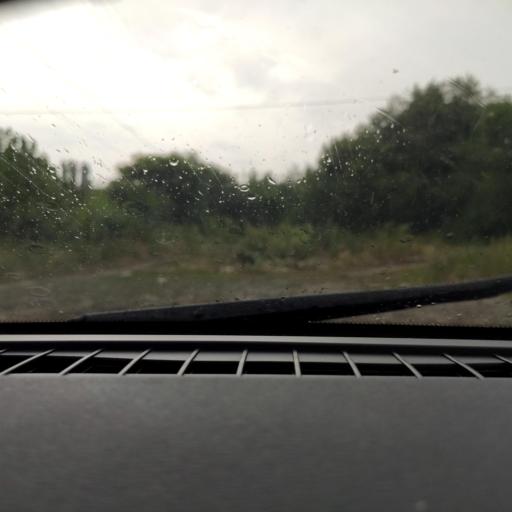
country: RU
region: Voronezj
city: Maslovka
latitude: 51.6430
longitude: 39.2810
